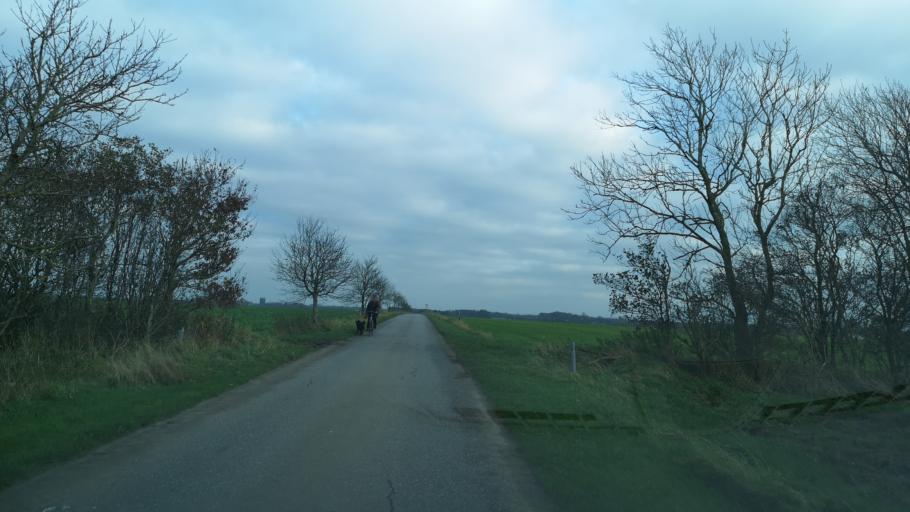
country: DK
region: Central Jutland
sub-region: Ringkobing-Skjern Kommune
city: Skjern
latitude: 55.9941
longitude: 8.5903
